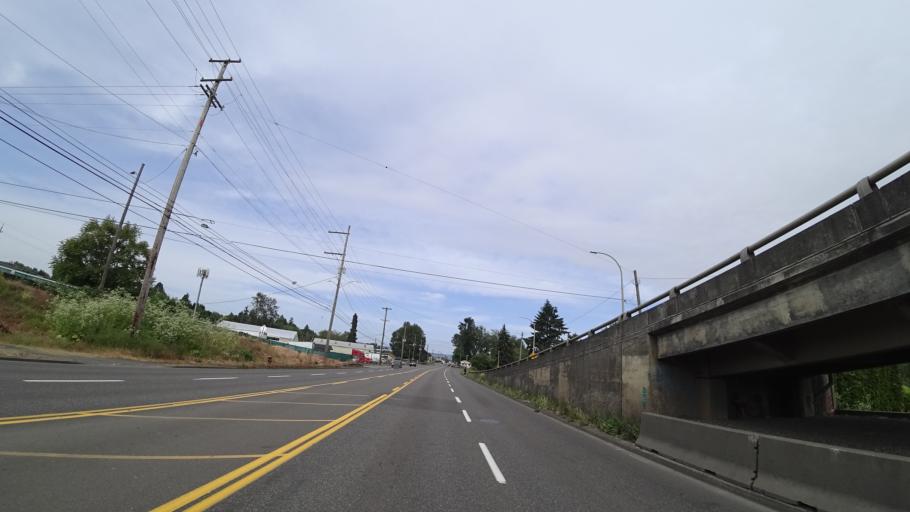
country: US
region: Oregon
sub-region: Multnomah County
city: Portland
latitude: 45.5736
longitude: -122.6302
